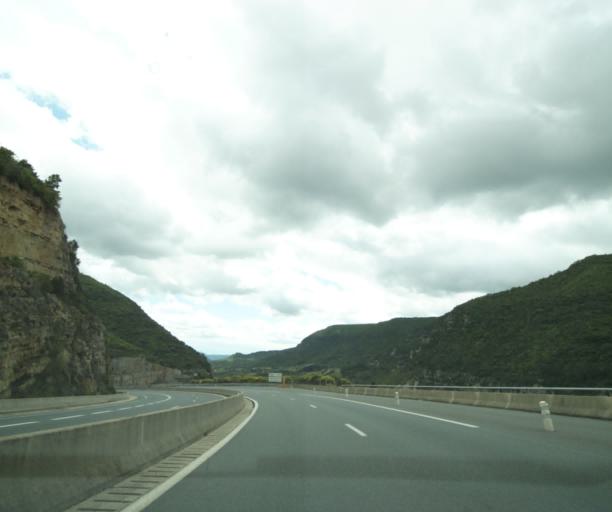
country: FR
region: Languedoc-Roussillon
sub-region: Departement de l'Herault
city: Lodeve
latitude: 43.8082
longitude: 3.3257
